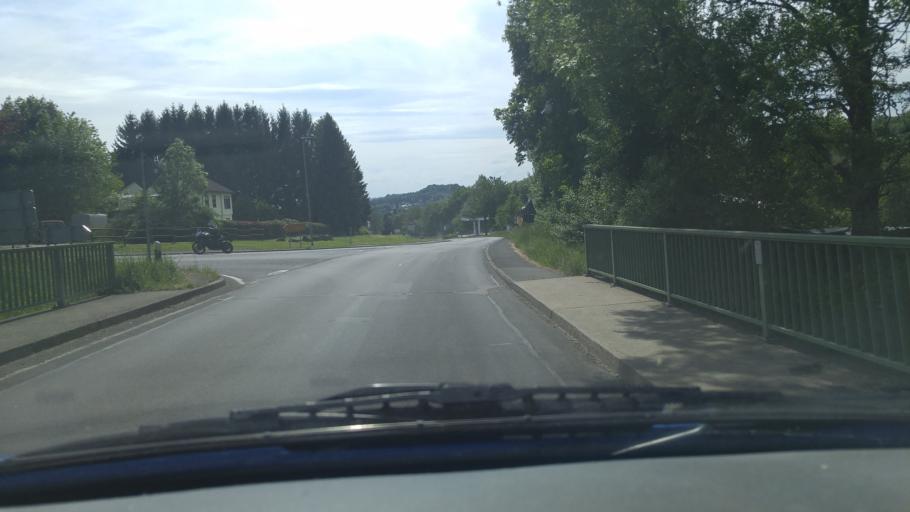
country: DE
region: Hesse
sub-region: Regierungsbezirk Giessen
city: Schotten
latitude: 50.5094
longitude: 9.1392
